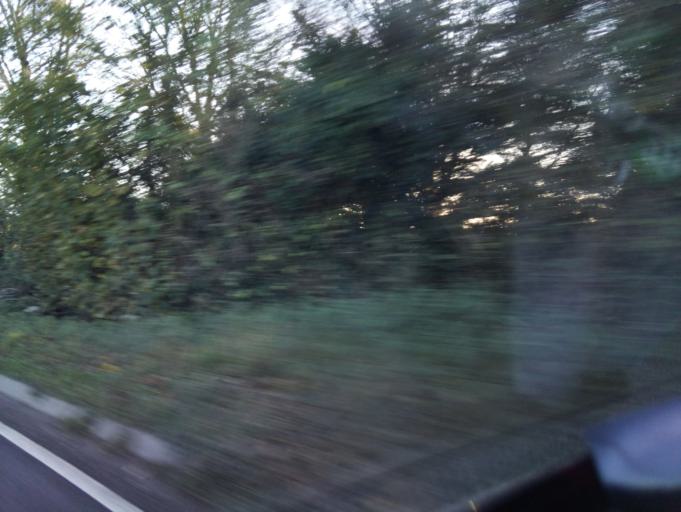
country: GB
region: England
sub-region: Wiltshire
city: Chicklade
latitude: 51.1281
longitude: -2.1633
